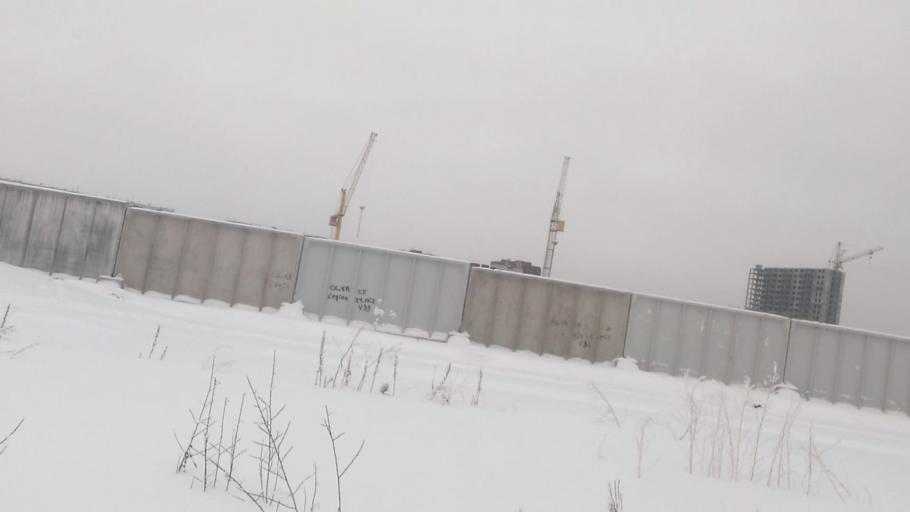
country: RU
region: Altai Krai
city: Novosilikatnyy
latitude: 53.3529
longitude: 83.6612
